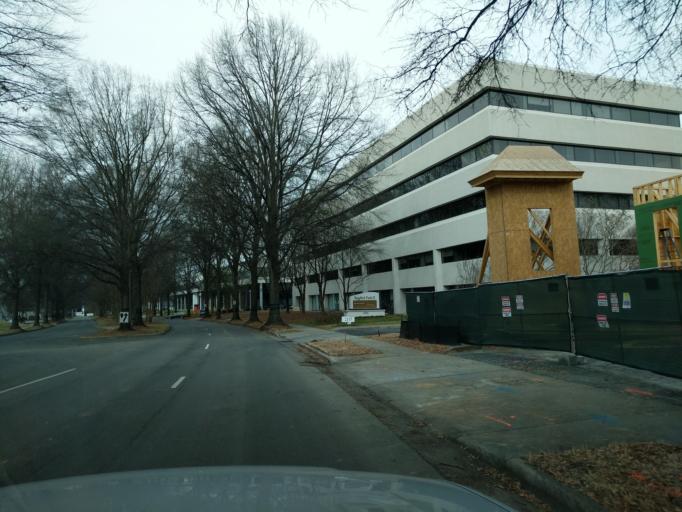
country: US
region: North Carolina
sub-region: Mecklenburg County
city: Charlotte
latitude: 35.1576
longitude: -80.8301
